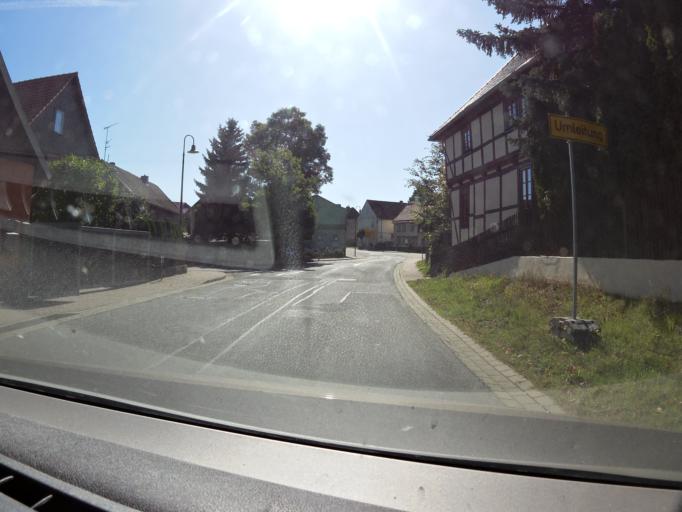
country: DE
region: Saxony-Anhalt
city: Friedrichsbrunn
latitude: 51.6795
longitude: 10.9680
